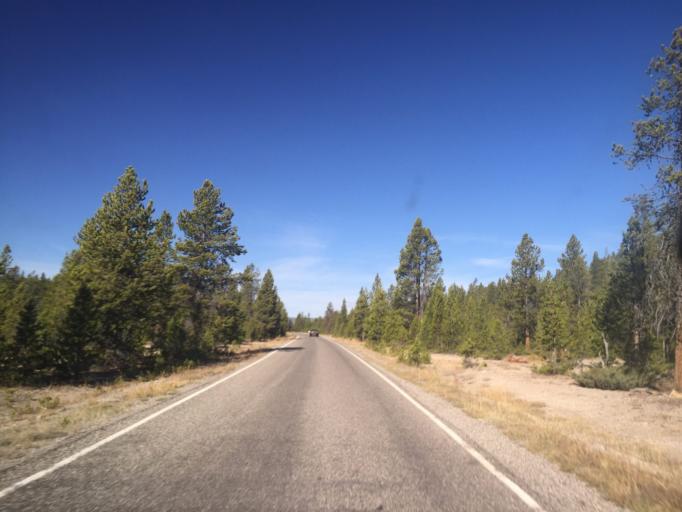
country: US
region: Montana
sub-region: Gallatin County
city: West Yellowstone
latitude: 44.5461
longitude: -110.7921
